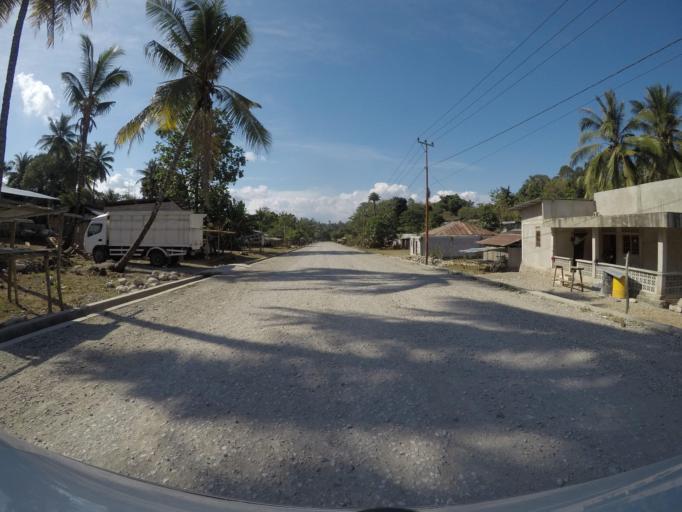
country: TL
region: Viqueque
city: Viqueque
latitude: -8.8360
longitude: 126.5189
